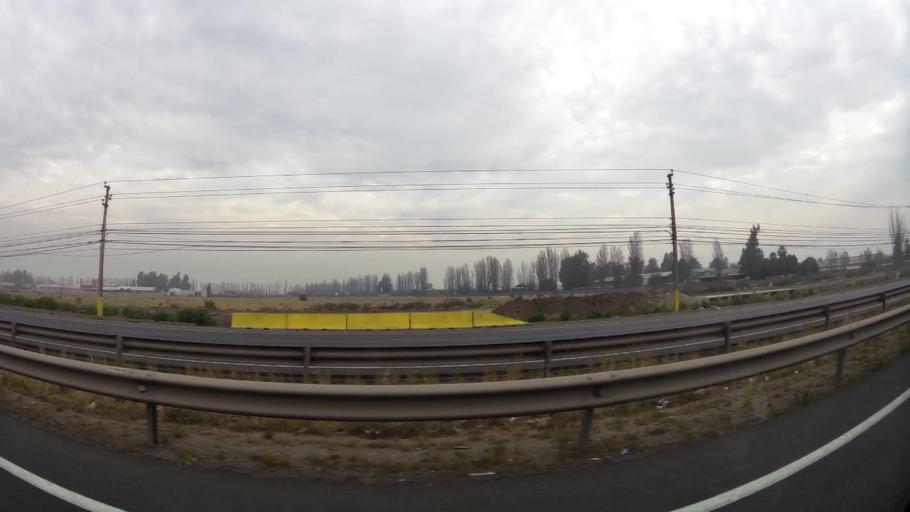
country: CL
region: Santiago Metropolitan
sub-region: Provincia de Chacabuco
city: Chicureo Abajo
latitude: -33.2845
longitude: -70.7368
